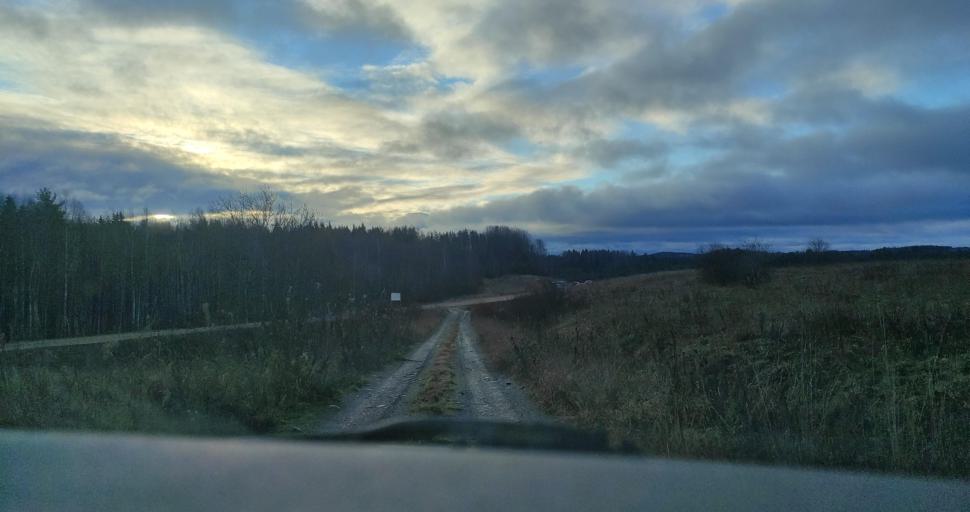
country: RU
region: Republic of Karelia
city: Pitkyaranta
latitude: 61.7267
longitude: 31.3837
